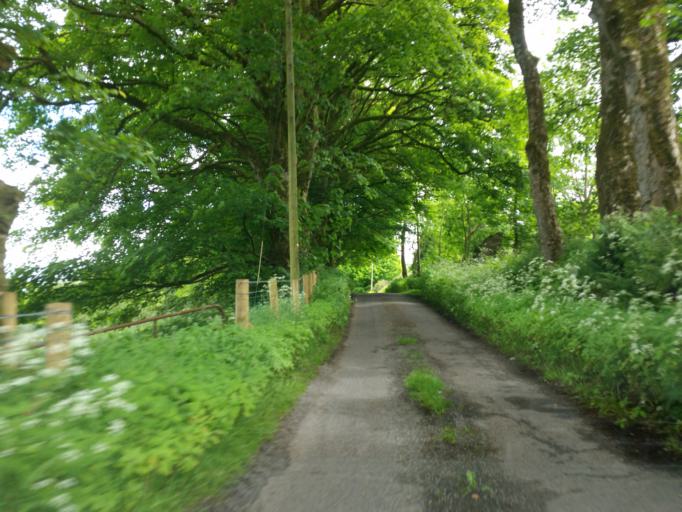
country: GB
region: Northern Ireland
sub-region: Omagh District
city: Omagh
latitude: 54.5576
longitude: -7.0742
